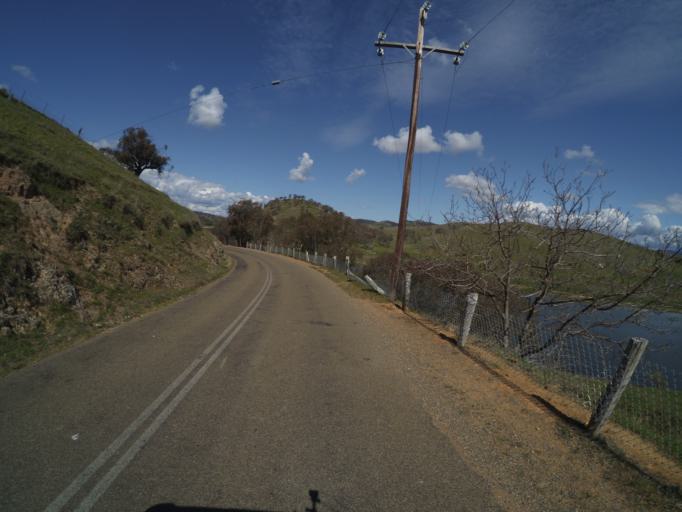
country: AU
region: New South Wales
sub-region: Yass Valley
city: Yass
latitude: -35.0021
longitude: 148.8461
